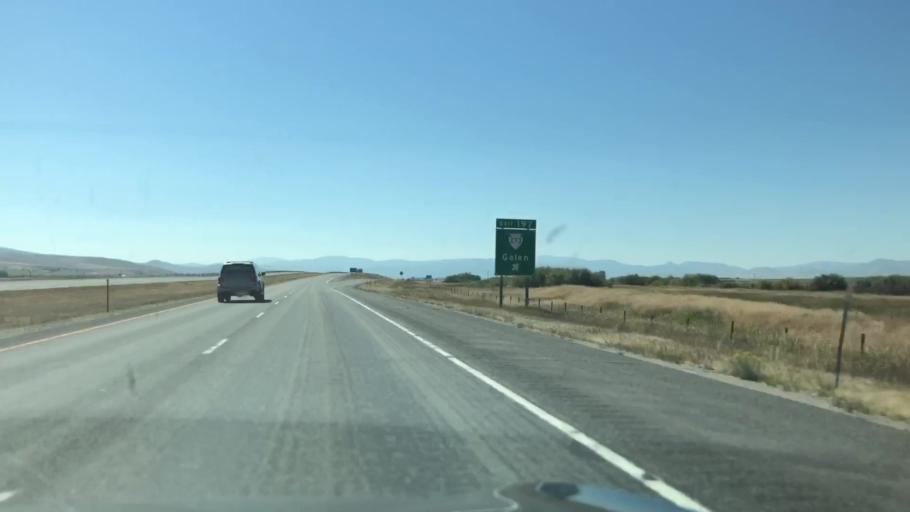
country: US
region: Montana
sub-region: Deer Lodge County
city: Warm Springs
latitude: 46.2428
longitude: -112.7648
